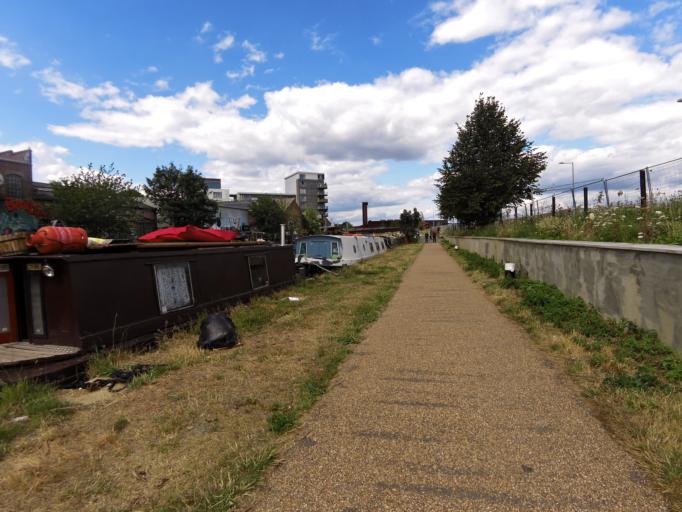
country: GB
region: England
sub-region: Greater London
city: Poplar
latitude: 51.5394
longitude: -0.0205
